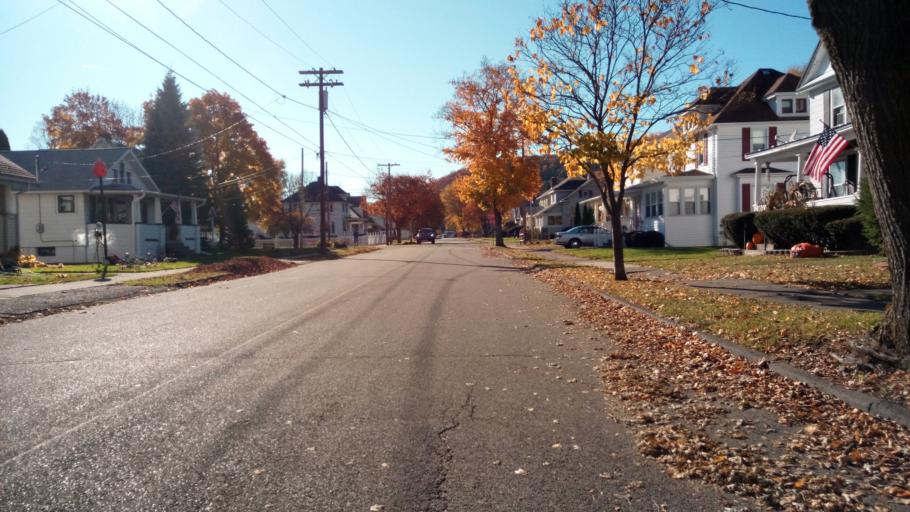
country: US
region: New York
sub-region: Chemung County
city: Southport
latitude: 42.0660
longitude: -76.8103
